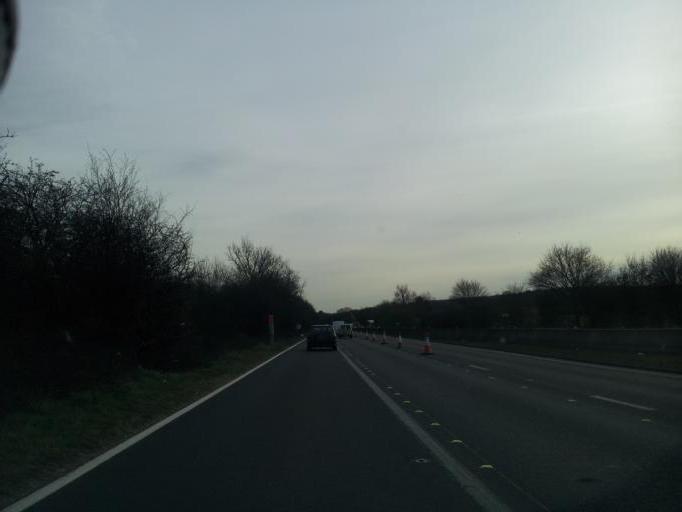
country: GB
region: England
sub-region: Hertfordshire
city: Hatfield
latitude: 51.7212
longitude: -0.2234
